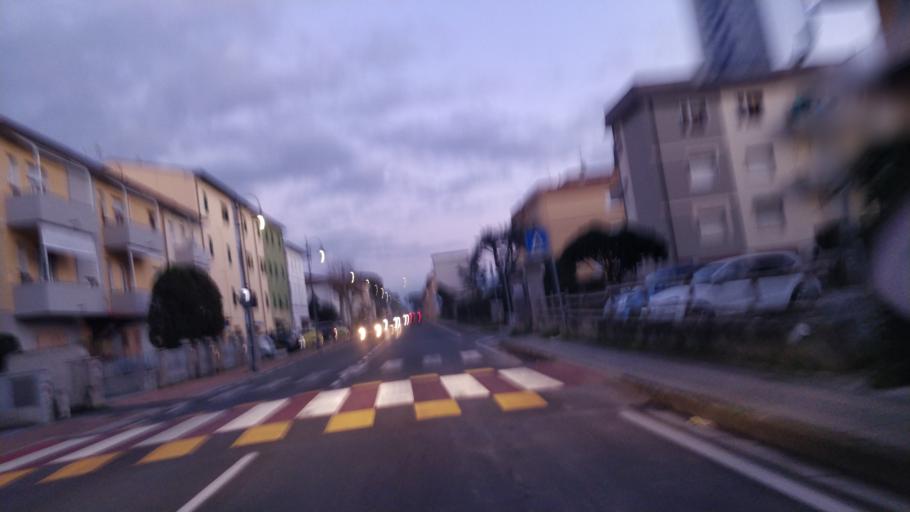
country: IT
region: Tuscany
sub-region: Provincia di Livorno
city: Vada
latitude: 43.3509
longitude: 10.4587
